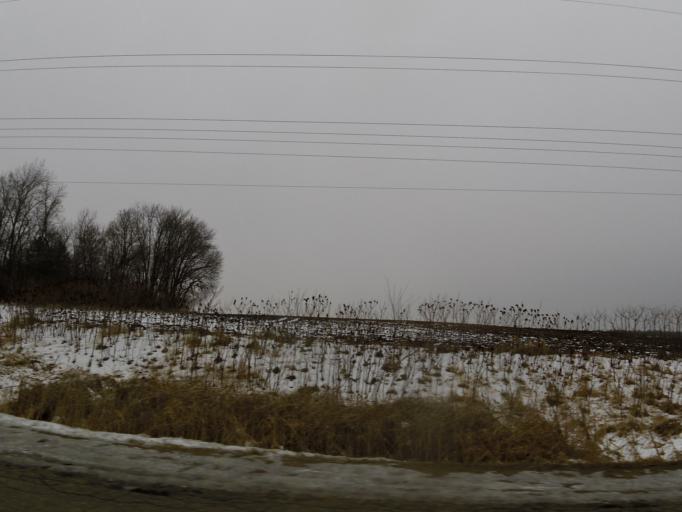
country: US
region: Minnesota
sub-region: Scott County
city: Jordan
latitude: 44.6401
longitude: -93.6204
